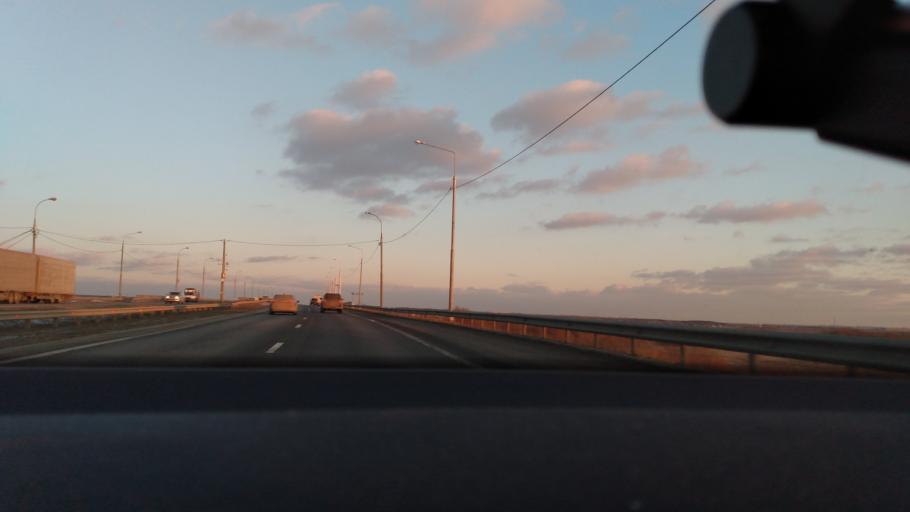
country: RU
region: Moskovskaya
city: Raduzhnyy
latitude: 55.1422
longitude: 38.7407
